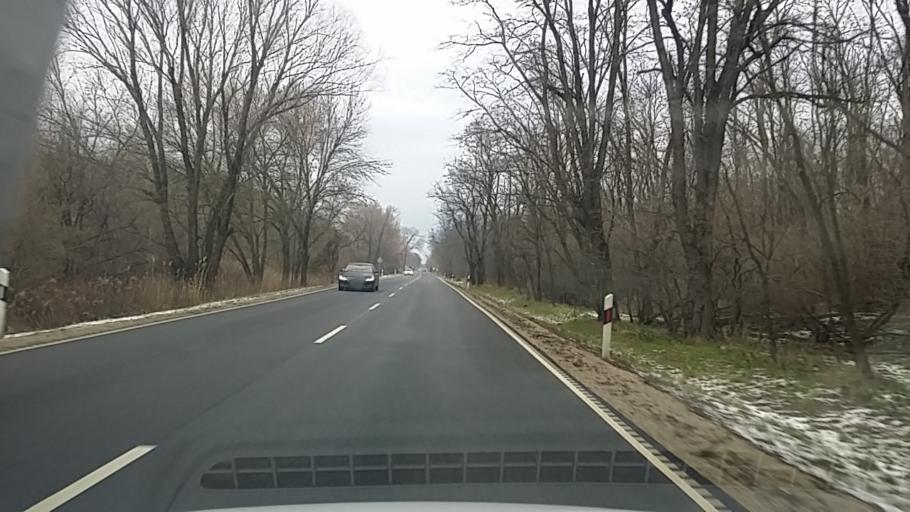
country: HU
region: Komarom-Esztergom
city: Csaszar
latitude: 47.4635
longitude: 18.0900
